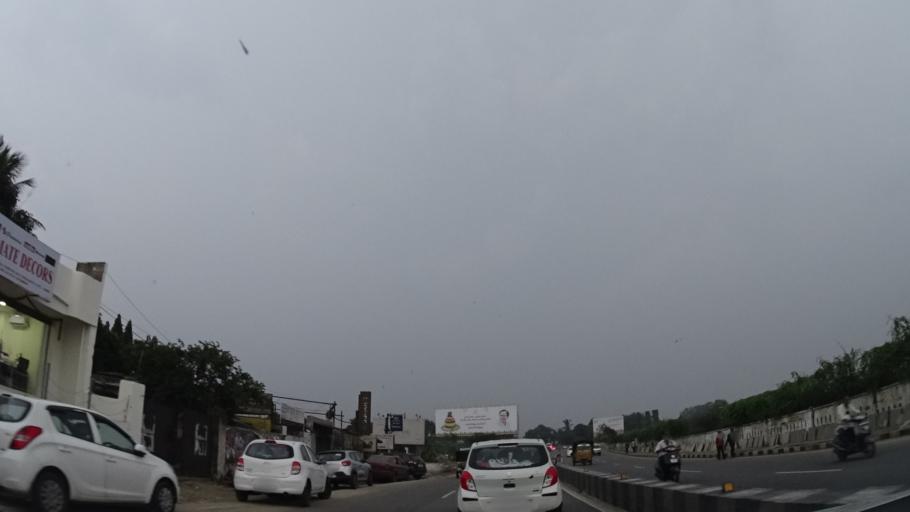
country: IN
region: Telangana
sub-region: Hyderabad
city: Malkajgiri
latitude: 17.4540
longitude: 78.4858
